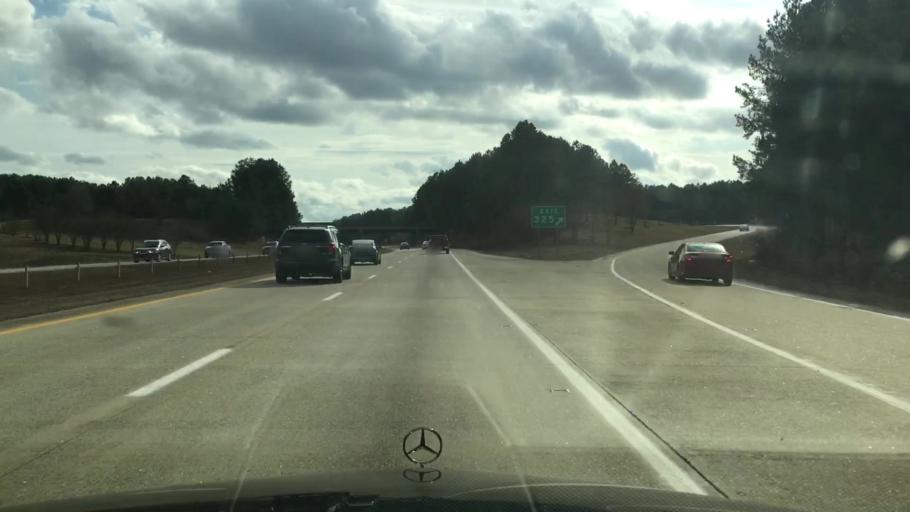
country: US
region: North Carolina
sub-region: Johnston County
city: Benson
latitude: 35.4255
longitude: -78.5311
